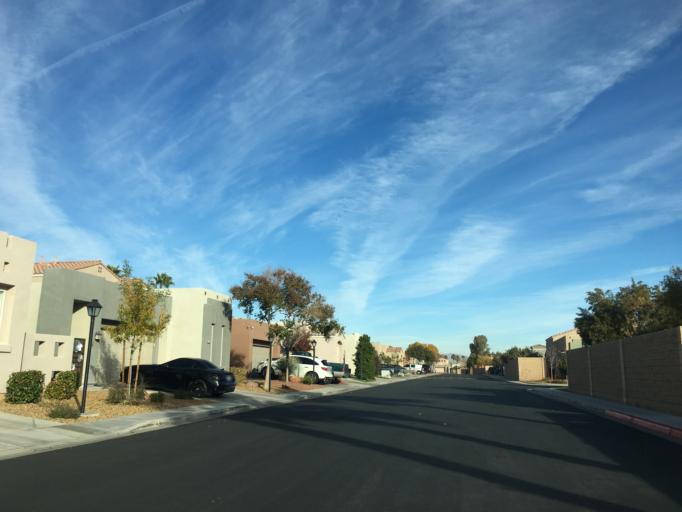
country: US
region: Nevada
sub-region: Clark County
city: Enterprise
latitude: 36.0217
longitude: -115.1674
